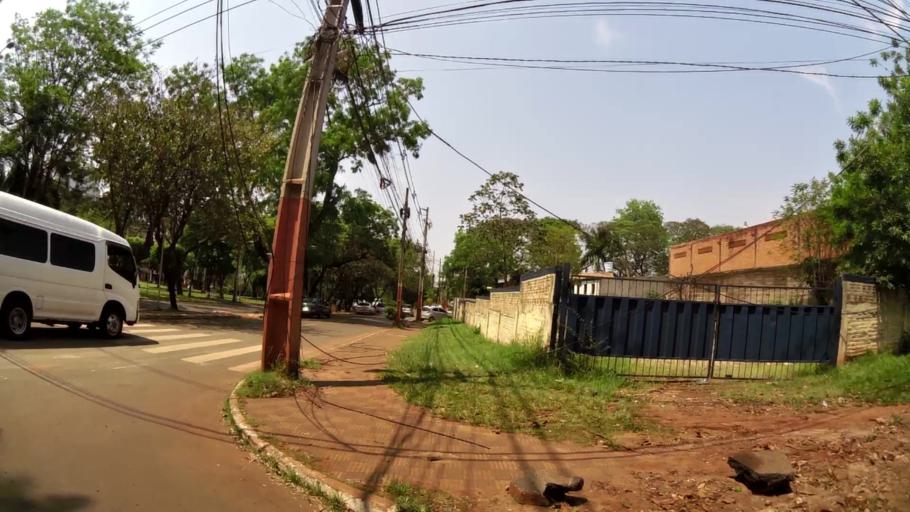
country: PY
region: Alto Parana
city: Ciudad del Este
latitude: -25.5178
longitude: -54.6089
